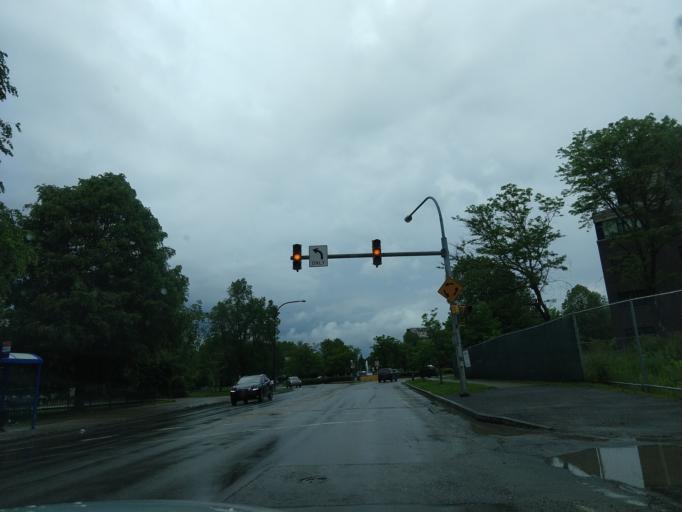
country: US
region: New York
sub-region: Erie County
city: Buffalo
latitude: 42.9194
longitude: -78.8680
